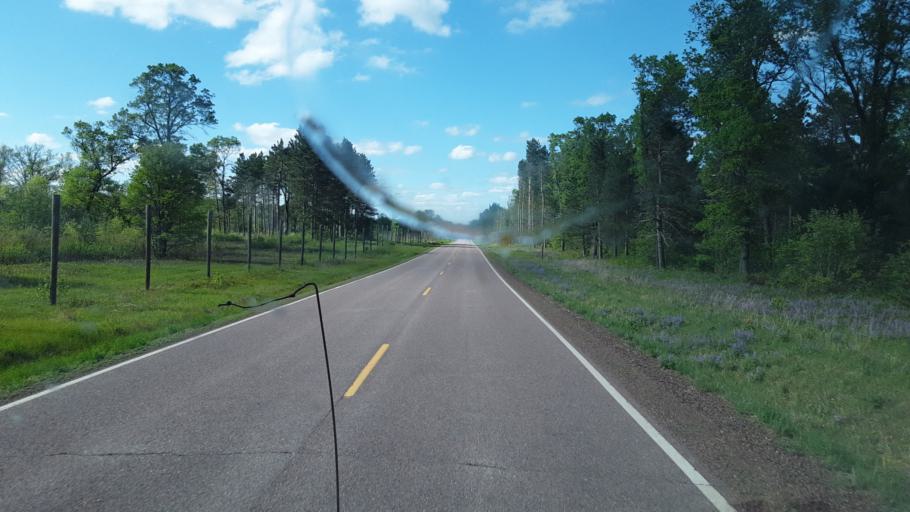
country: US
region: Wisconsin
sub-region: Wood County
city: Nekoosa
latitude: 44.3423
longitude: -90.1306
